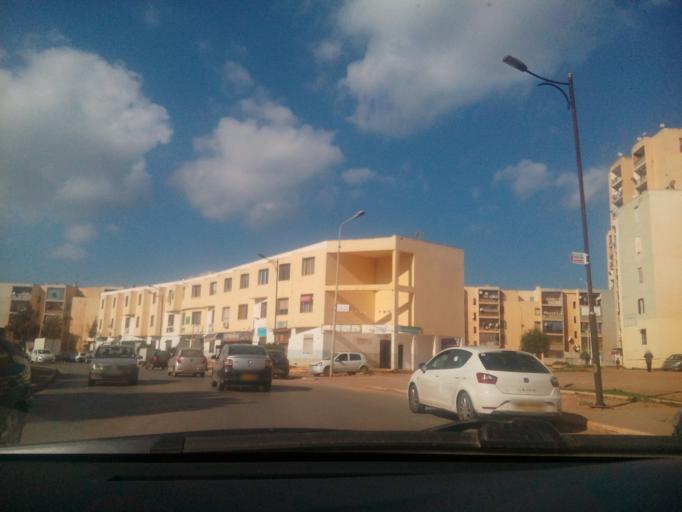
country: DZ
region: Oran
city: Oran
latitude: 35.7036
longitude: -0.5995
